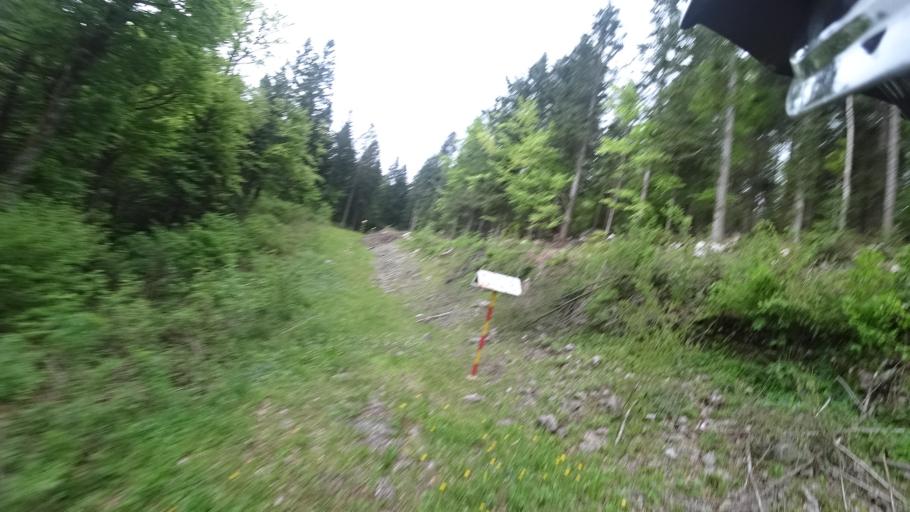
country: HR
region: Karlovacka
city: Plaski
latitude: 44.9569
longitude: 15.4144
